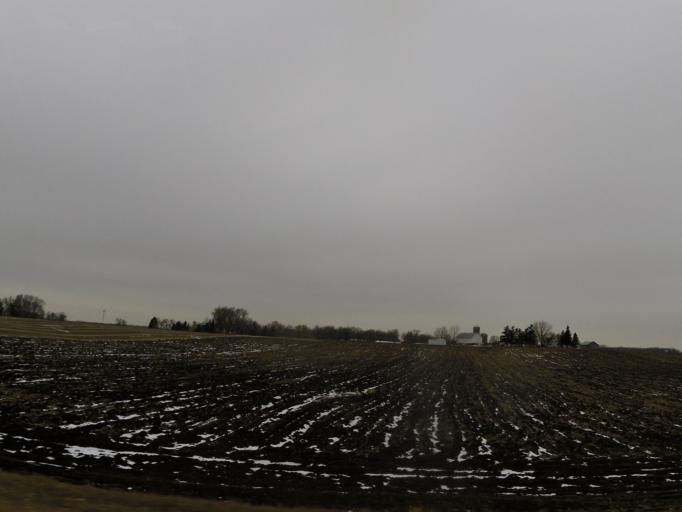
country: US
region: Minnesota
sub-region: Carver County
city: Carver
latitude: 44.7706
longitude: -93.6838
